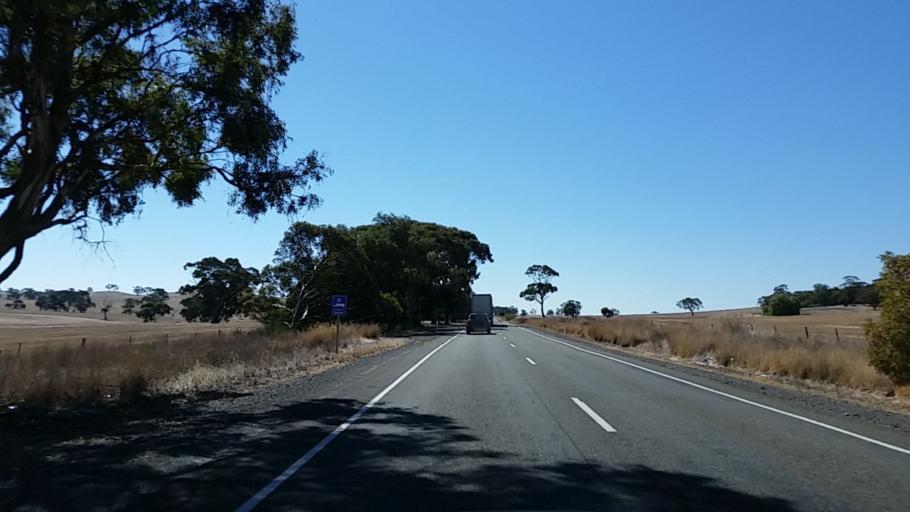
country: AU
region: South Australia
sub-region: Clare and Gilbert Valleys
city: Clare
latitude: -34.0494
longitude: 138.7974
